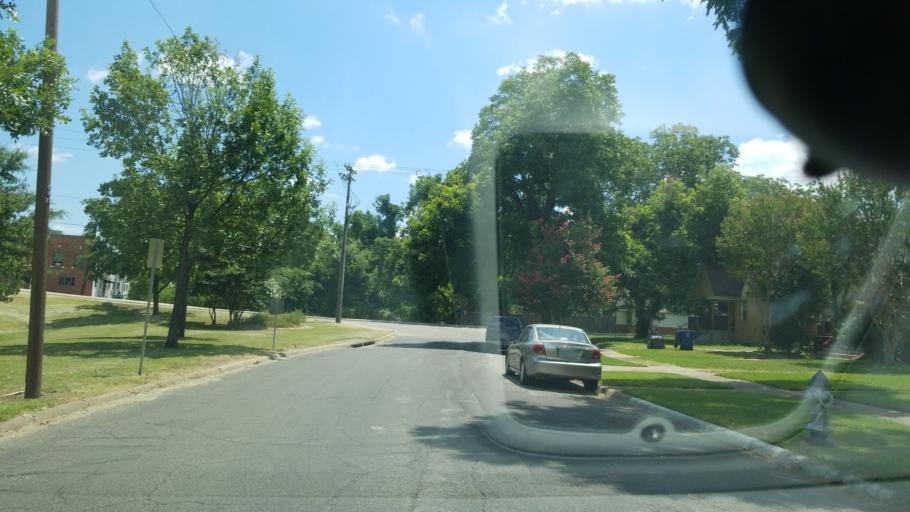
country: US
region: Texas
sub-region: Dallas County
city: Cockrell Hill
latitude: 32.7320
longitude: -96.8407
